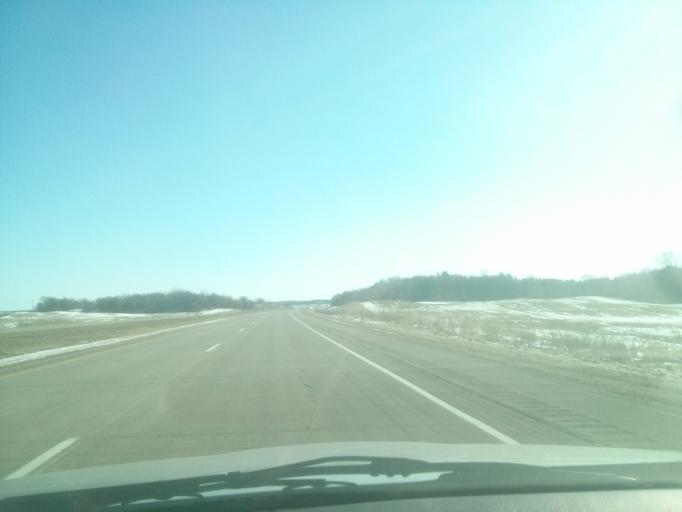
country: US
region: Wisconsin
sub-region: Saint Croix County
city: Somerset
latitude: 45.1089
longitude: -92.6873
